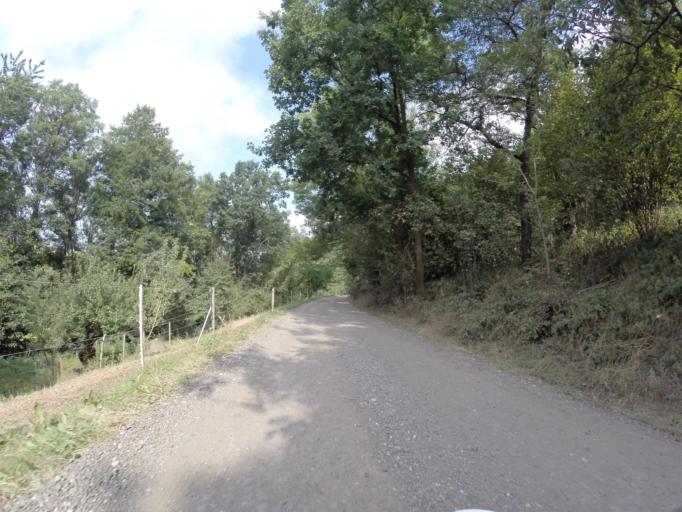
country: DE
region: Thuringia
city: Schloben
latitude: 50.8892
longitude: 11.6948
